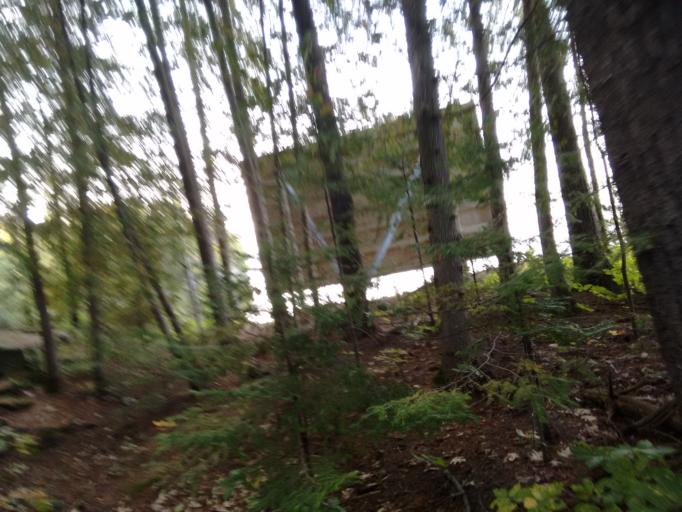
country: CA
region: Ontario
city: Arnprior
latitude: 45.4637
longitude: -76.2561
